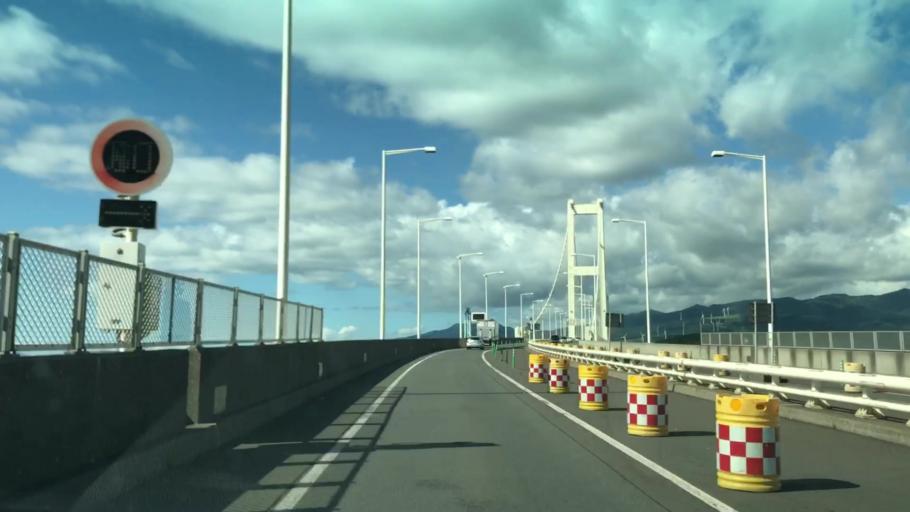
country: JP
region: Hokkaido
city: Muroran
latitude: 42.3448
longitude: 140.9490
